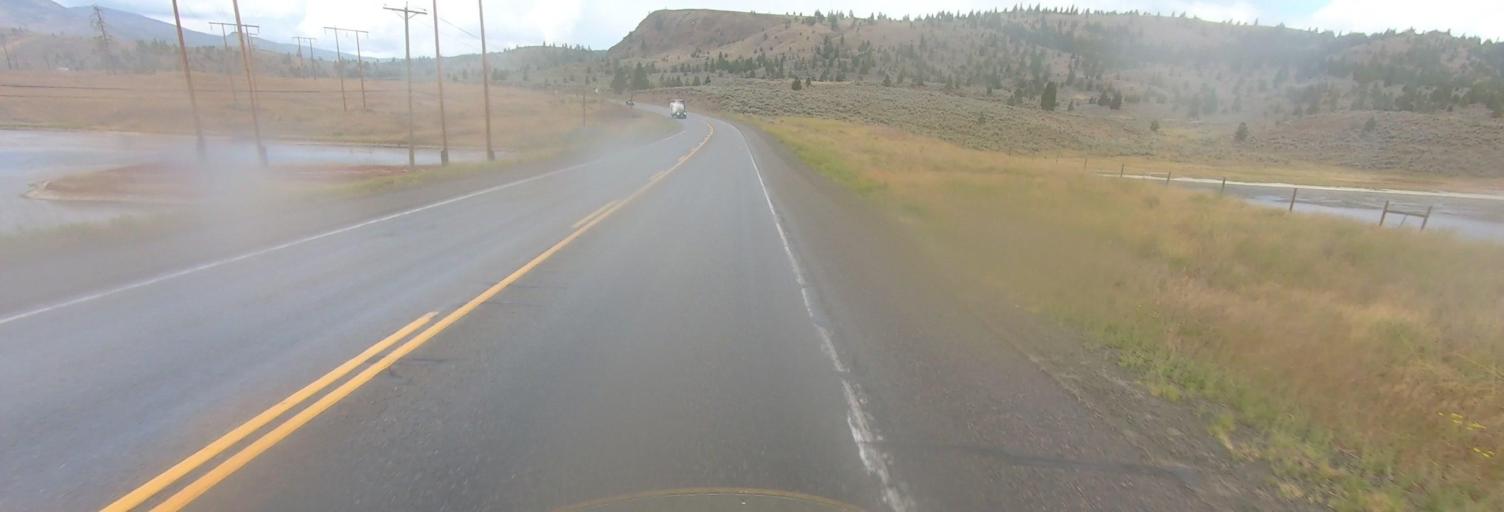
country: CA
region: British Columbia
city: Kamloops
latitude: 50.6683
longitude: -120.5125
